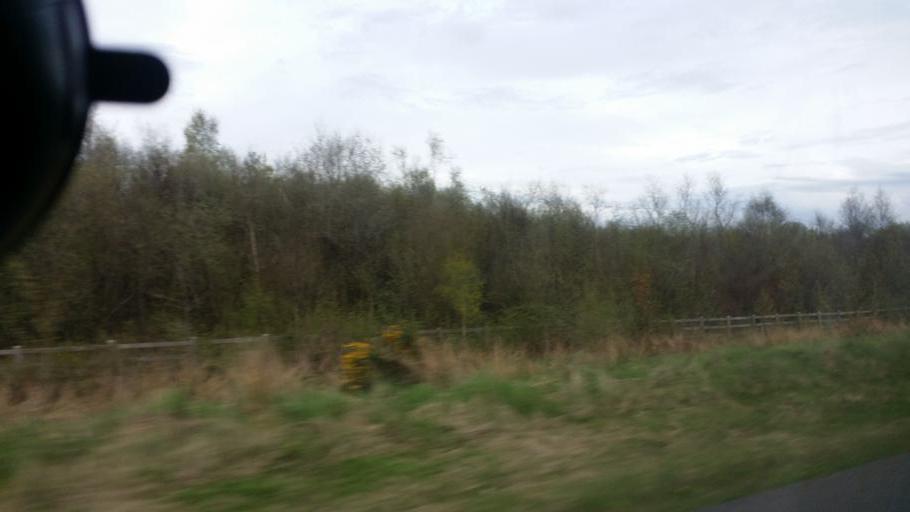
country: IE
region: Ulster
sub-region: An Cabhan
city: Belturbet
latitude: 54.0852
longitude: -7.4418
